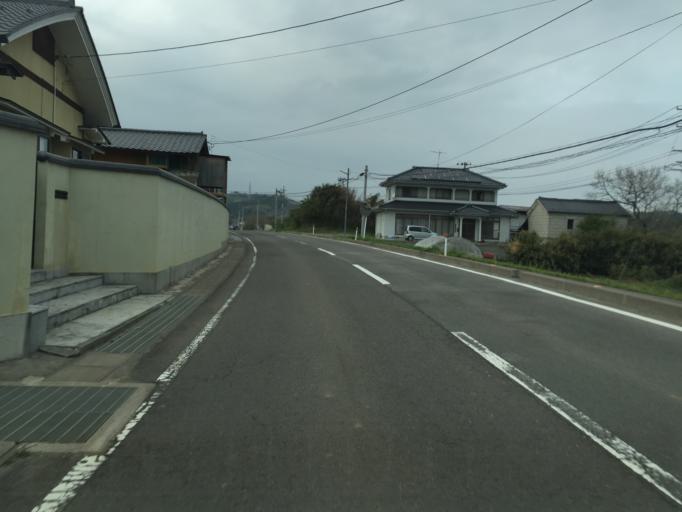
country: JP
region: Fukushima
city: Nihommatsu
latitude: 37.6588
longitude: 140.4240
